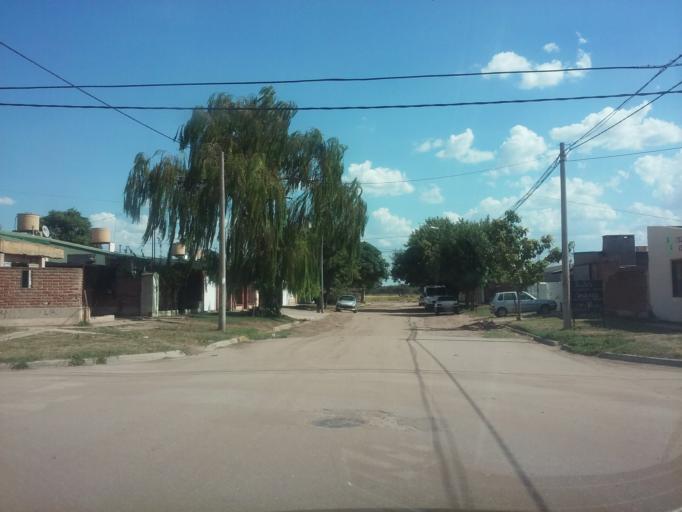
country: AR
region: La Pampa
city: Santa Rosa
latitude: -36.6480
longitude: -64.2959
